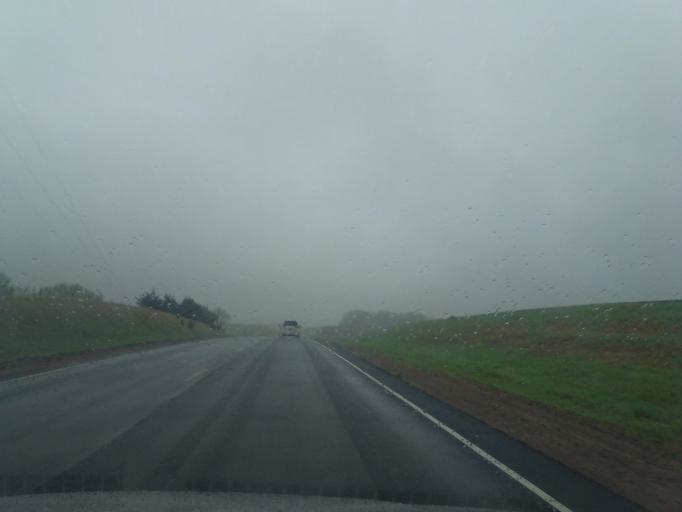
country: US
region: Nebraska
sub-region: Wayne County
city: Wayne
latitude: 42.1905
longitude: -97.1749
